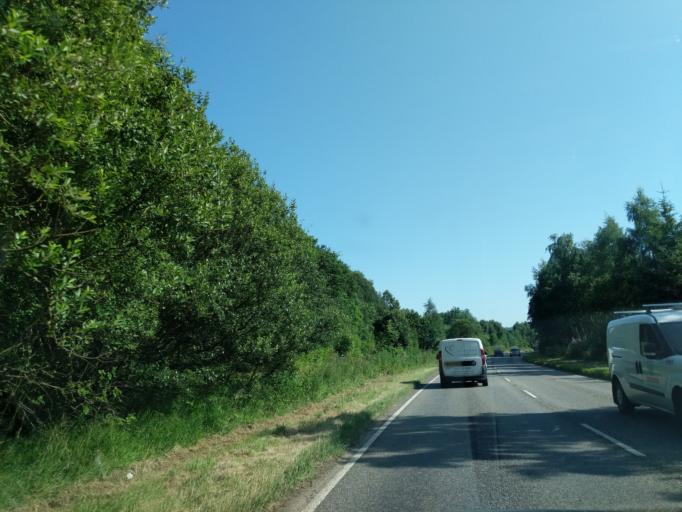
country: GB
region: Scotland
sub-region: Moray
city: Rothes
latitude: 57.5039
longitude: -3.1943
